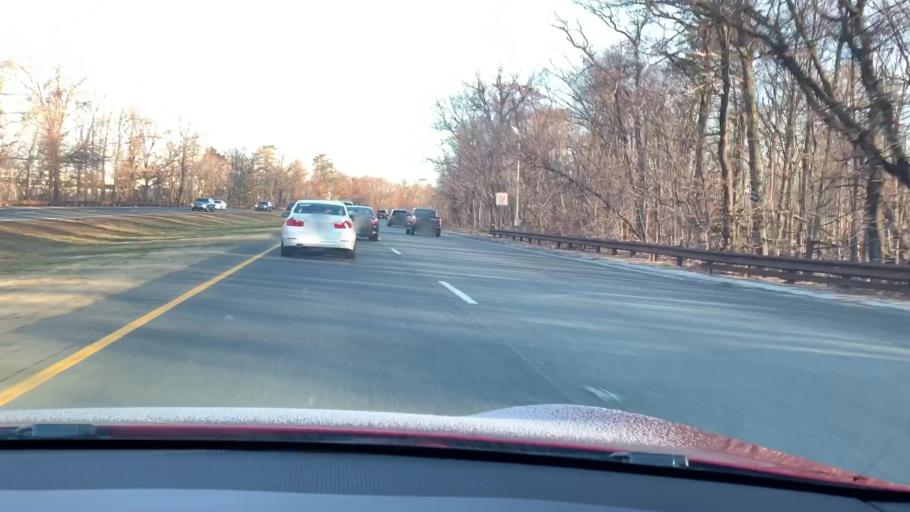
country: US
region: New Jersey
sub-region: Bergen County
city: Englewood Cliffs
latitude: 40.8683
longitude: -73.9540
